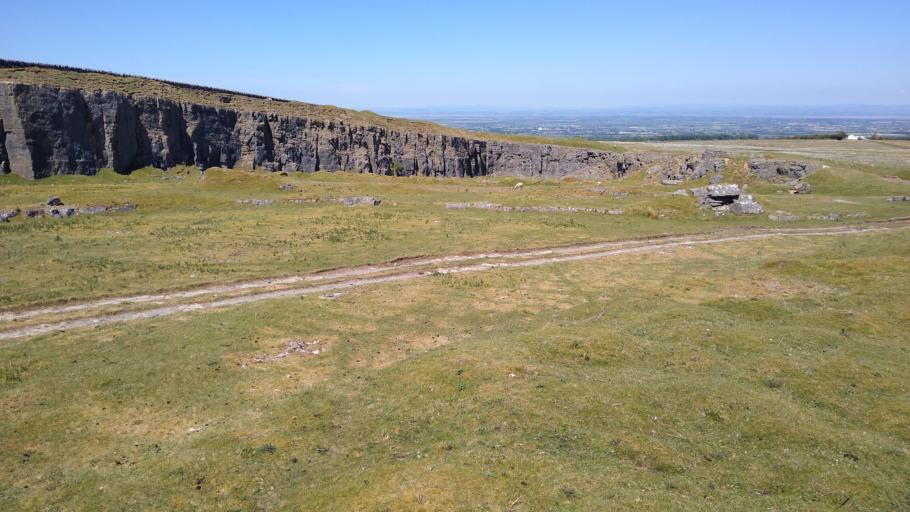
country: GB
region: England
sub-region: Cumbria
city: Wigton
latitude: 54.7505
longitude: -3.1143
